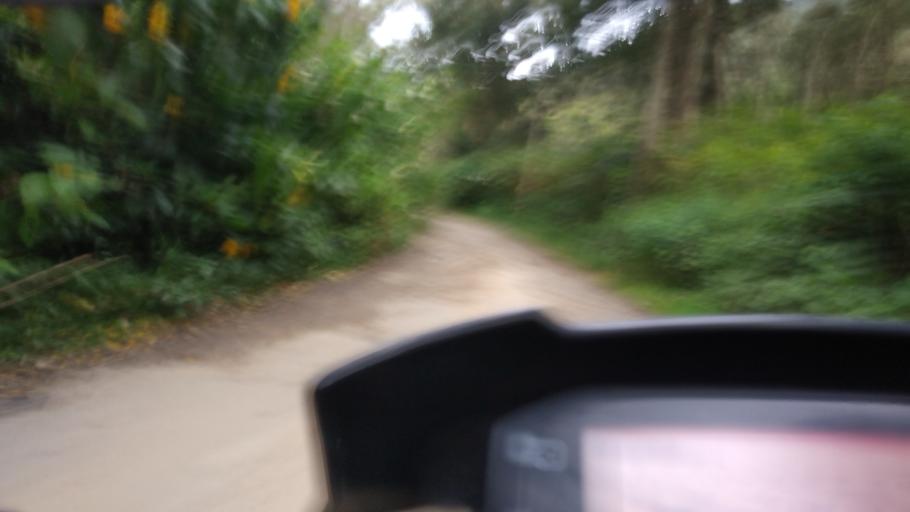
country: IN
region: Tamil Nadu
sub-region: Theni
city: Bodinayakkanur
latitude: 10.0238
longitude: 77.2479
